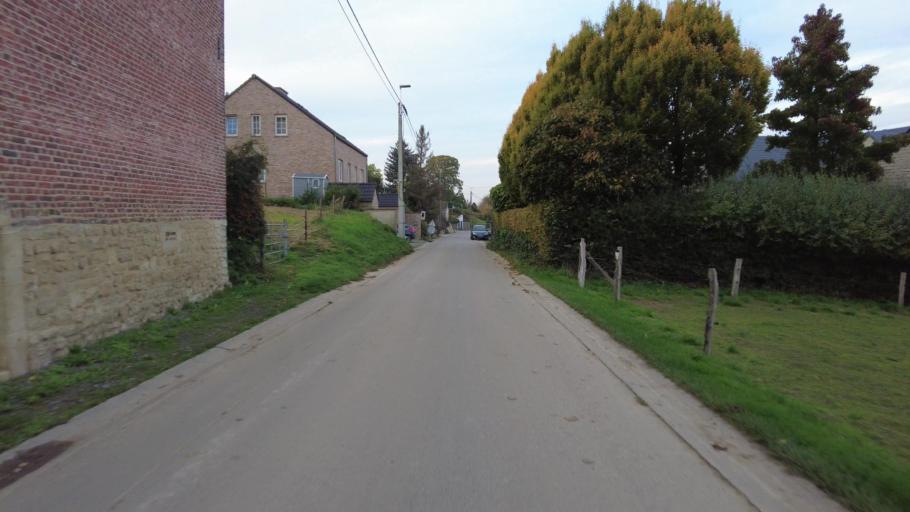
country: BE
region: Wallonia
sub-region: Province du Brabant Wallon
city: Jodoigne
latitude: 50.7426
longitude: 4.8714
